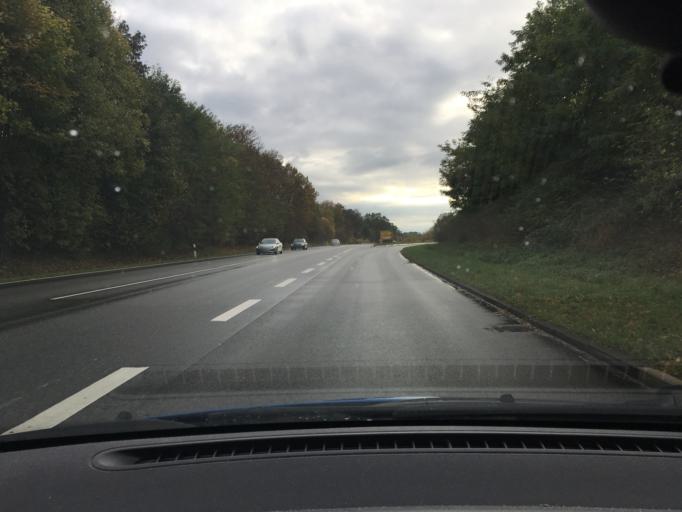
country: DE
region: Schleswig-Holstein
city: Alt Molln
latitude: 53.6245
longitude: 10.6671
